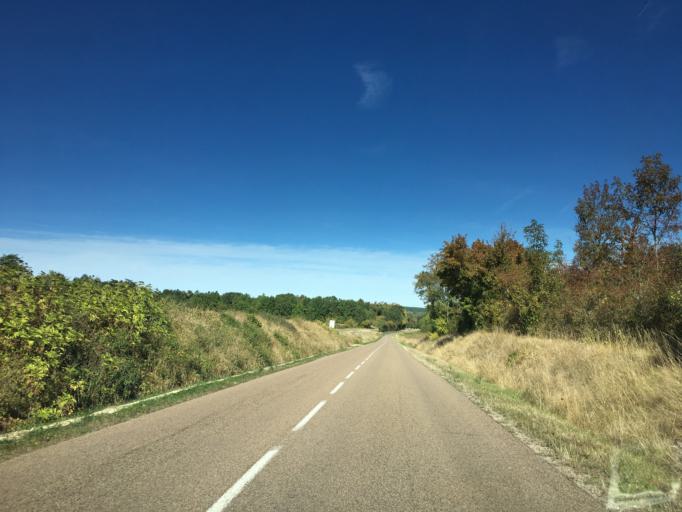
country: FR
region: Bourgogne
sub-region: Departement de l'Yonne
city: Vermenton
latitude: 47.6125
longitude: 3.6768
